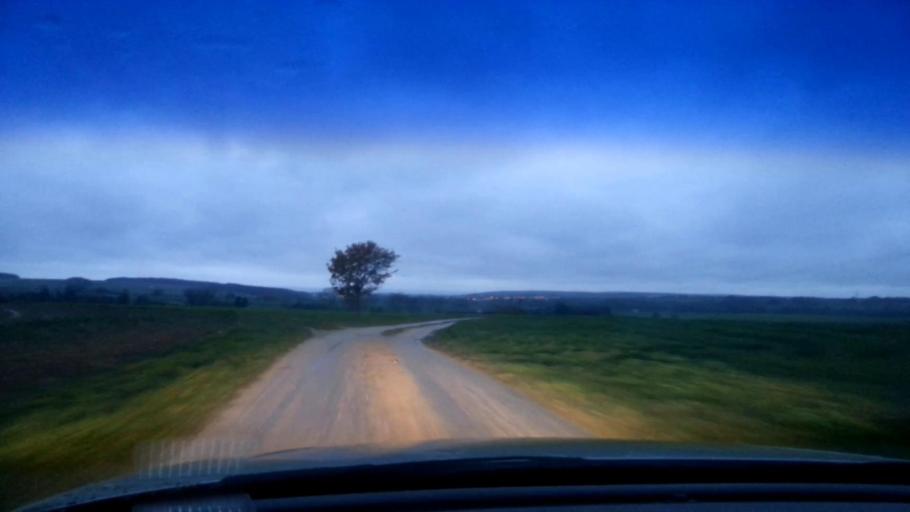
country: DE
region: Bavaria
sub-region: Upper Franconia
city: Schesslitz
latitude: 49.9504
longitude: 11.0127
